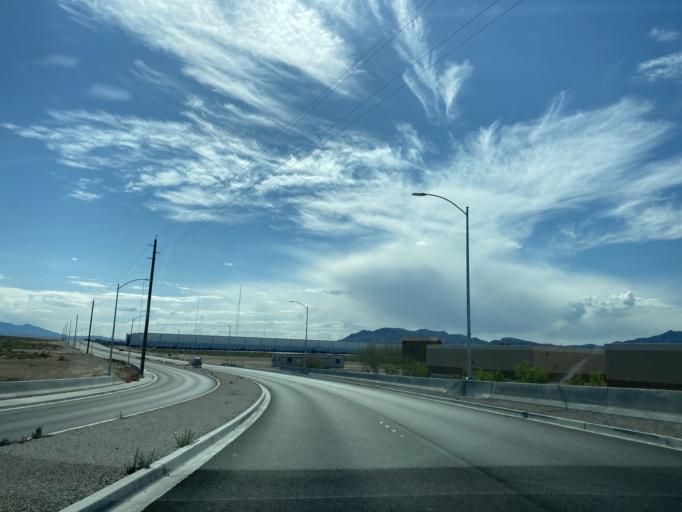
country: US
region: Nevada
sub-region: Clark County
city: Nellis Air Force Base
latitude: 36.2702
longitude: -115.0549
